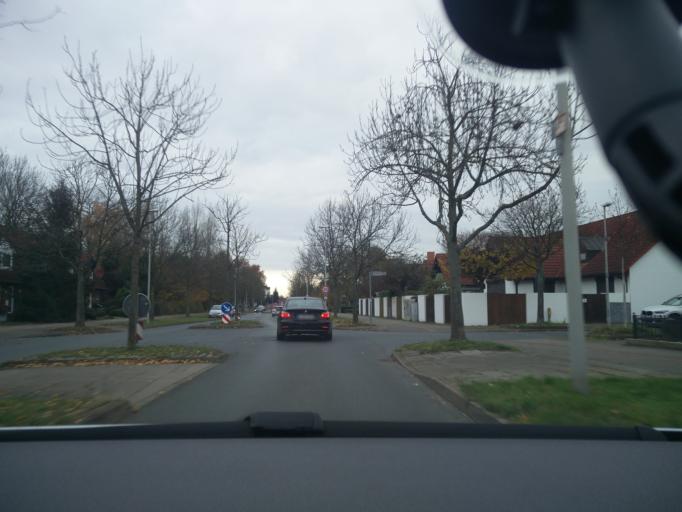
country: DE
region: Lower Saxony
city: Laatzen
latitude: 52.3428
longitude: 9.8214
